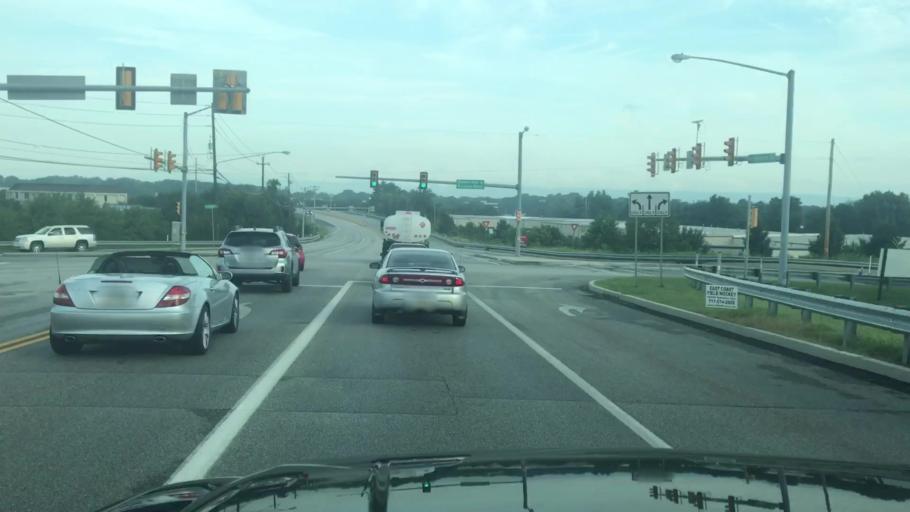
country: US
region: Pennsylvania
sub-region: Cumberland County
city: Shiremanstown
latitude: 40.2045
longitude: -76.9544
